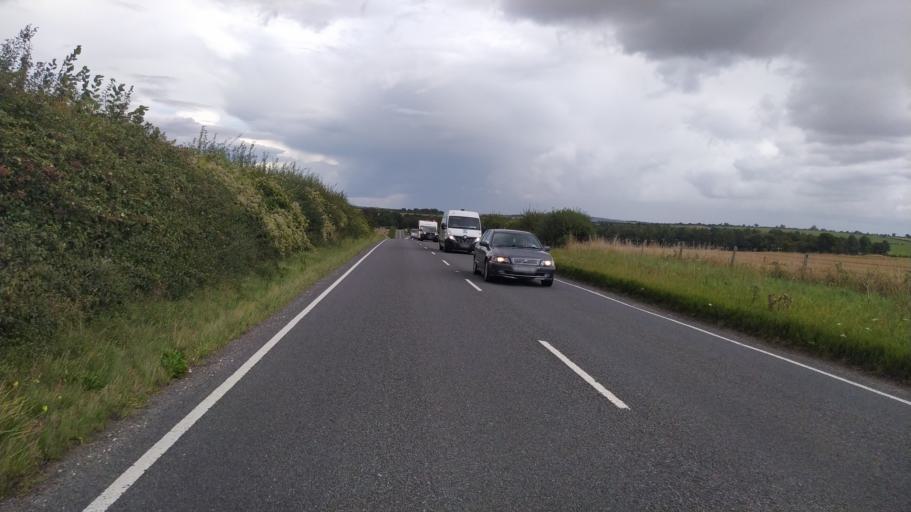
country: GB
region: England
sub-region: Dorset
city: Blandford Forum
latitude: 50.9059
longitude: -2.0712
